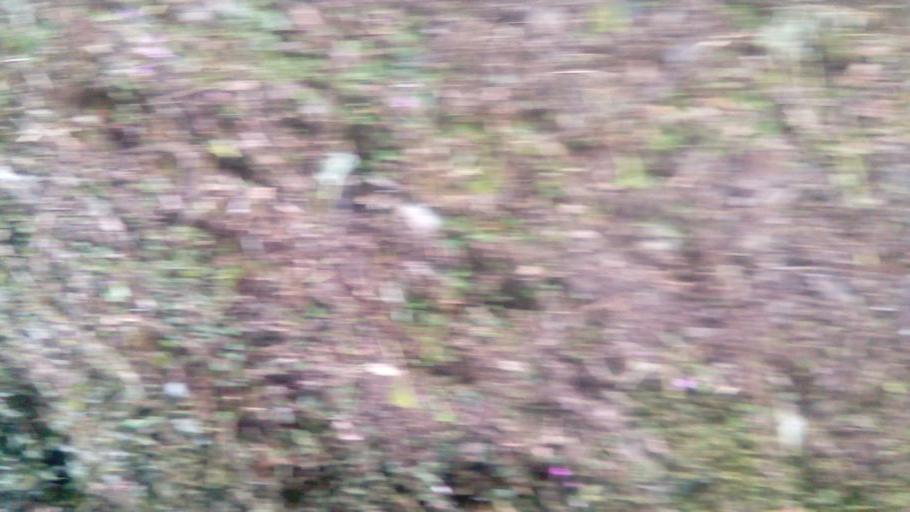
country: TW
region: Taiwan
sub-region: Yilan
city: Yilan
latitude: 24.5497
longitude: 121.4583
